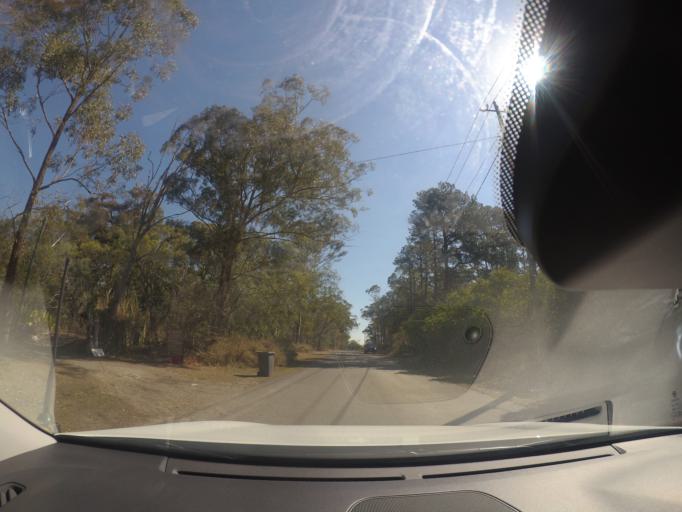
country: AU
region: Queensland
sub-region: Logan
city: Woodridge
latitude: -27.6417
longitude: 153.0907
